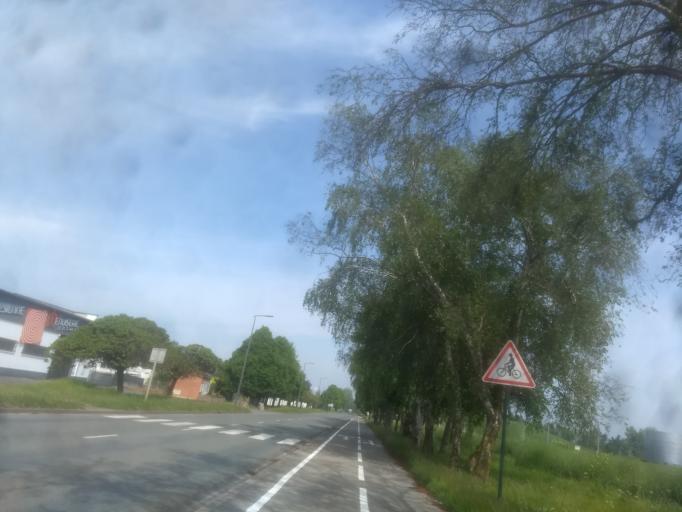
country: FR
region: Nord-Pas-de-Calais
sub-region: Departement du Pas-de-Calais
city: Tilloy-les-Mofflaines
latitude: 50.2836
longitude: 2.8130
